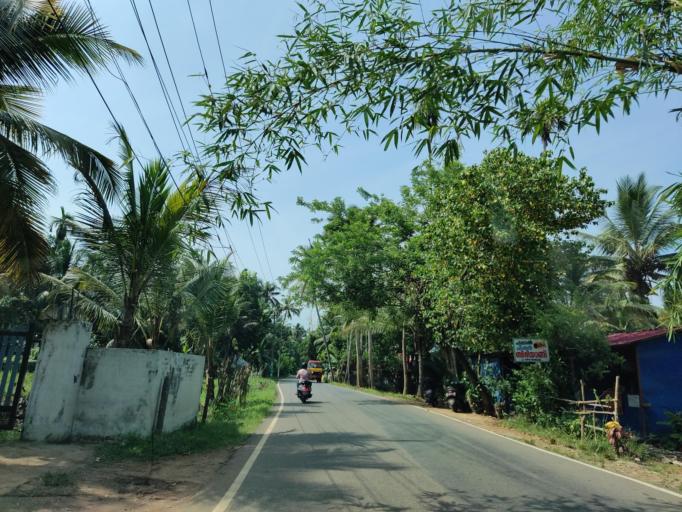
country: IN
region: Kerala
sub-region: Alappuzha
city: Mavelikara
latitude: 9.3328
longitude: 76.4680
